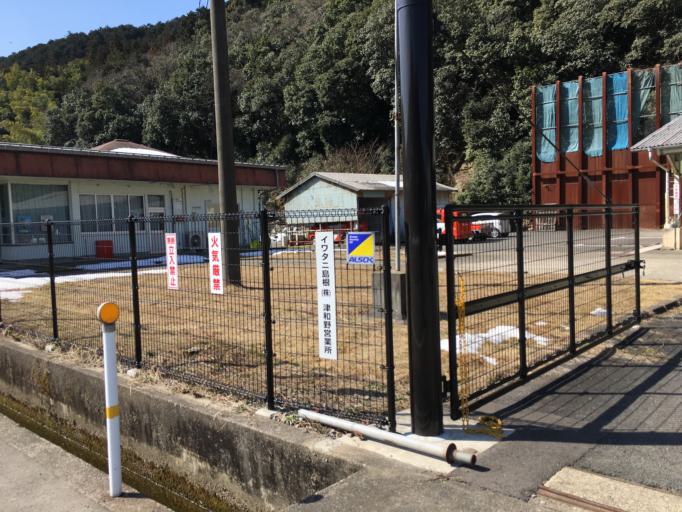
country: JP
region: Shimane
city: Masuda
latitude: 34.4572
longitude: 131.7668
